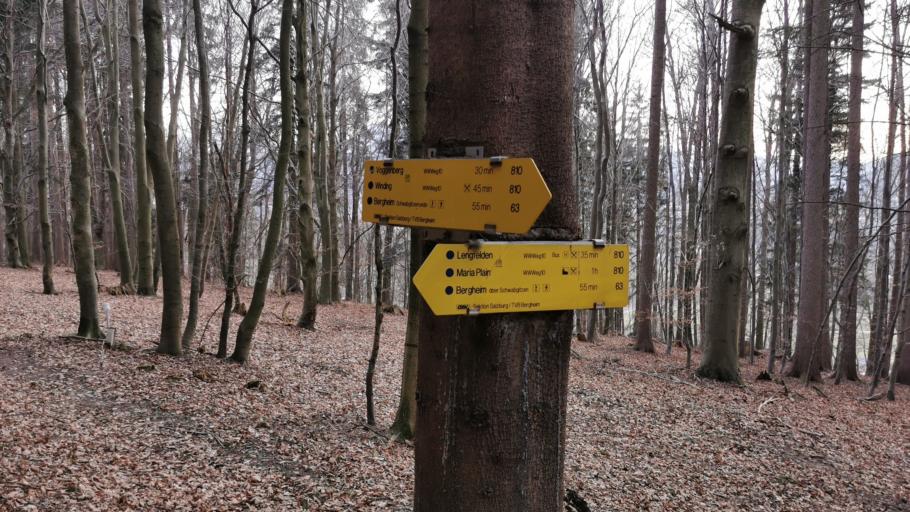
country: AT
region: Salzburg
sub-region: Politischer Bezirk Salzburg-Umgebung
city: Bergheim
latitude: 47.8536
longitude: 13.0310
